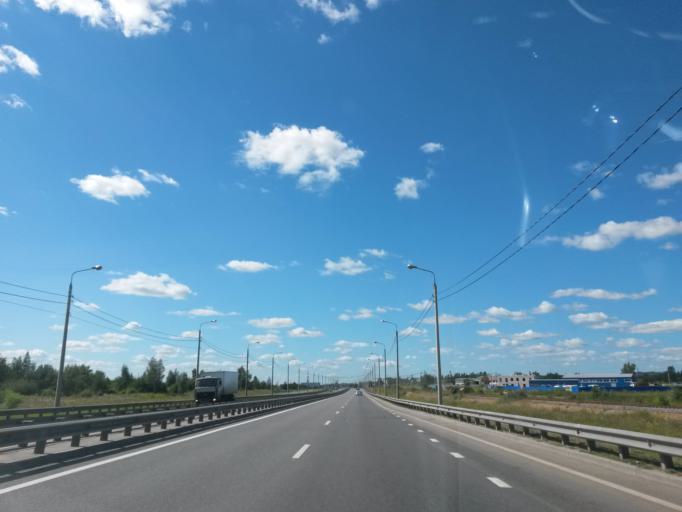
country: RU
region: Jaroslavl
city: Yaroslavl
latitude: 57.6684
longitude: 39.8082
